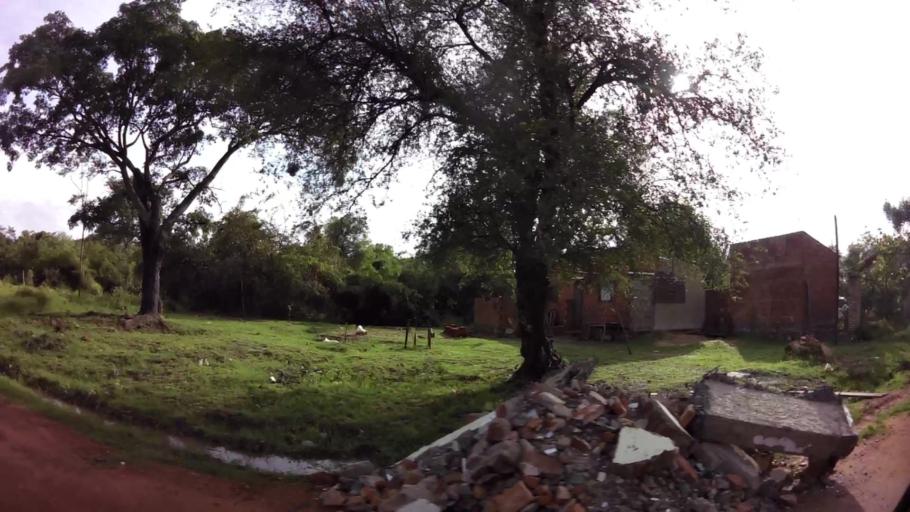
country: PY
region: Central
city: Limpio
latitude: -25.1853
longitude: -57.4808
